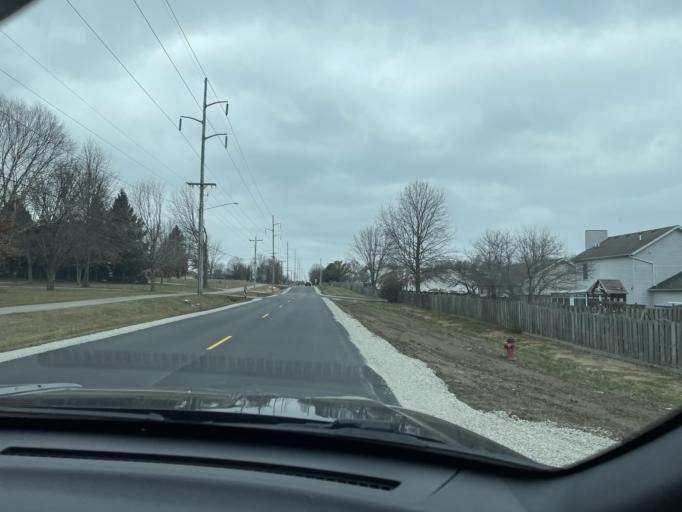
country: US
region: Illinois
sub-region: Sangamon County
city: Rochester
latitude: 39.7689
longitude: -89.5788
